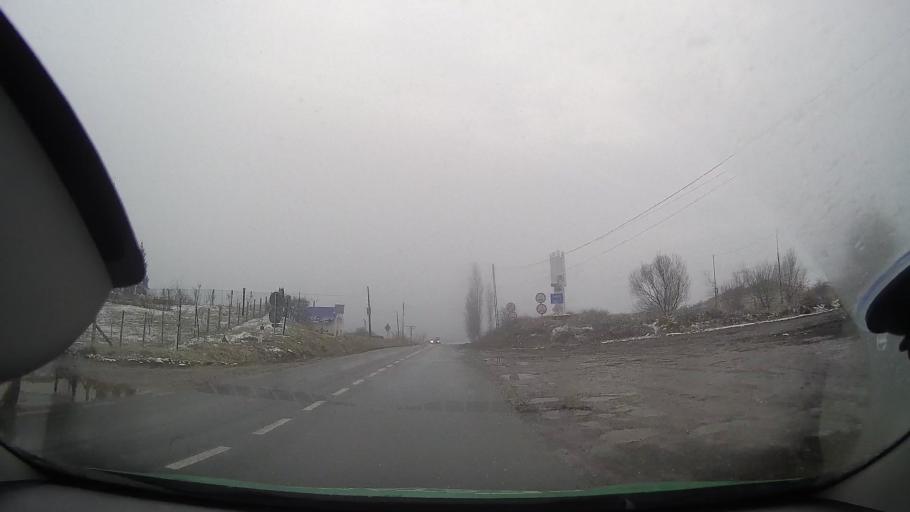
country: RO
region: Sibiu
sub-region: Comuna Blajel
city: Blajel
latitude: 46.2552
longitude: 24.2994
